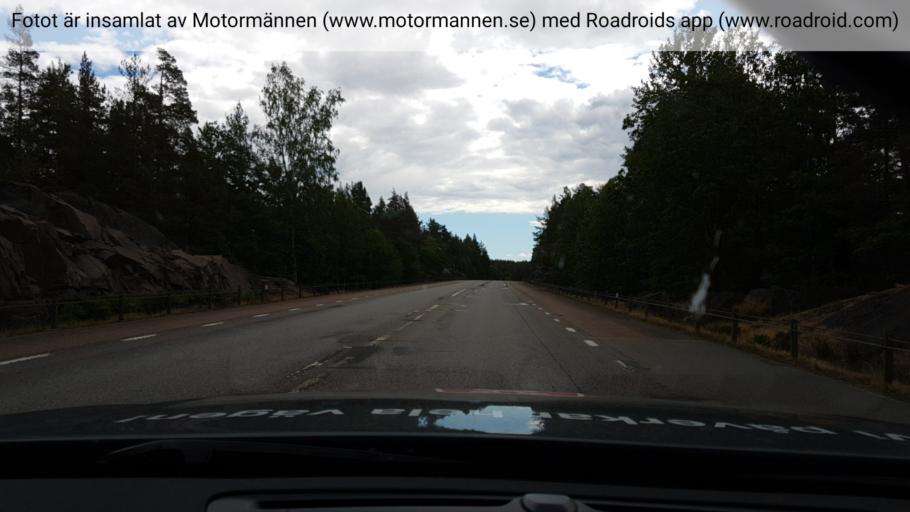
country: SE
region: Kalmar
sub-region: Vasterviks Kommun
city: Ankarsrum
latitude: 57.6363
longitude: 16.4515
